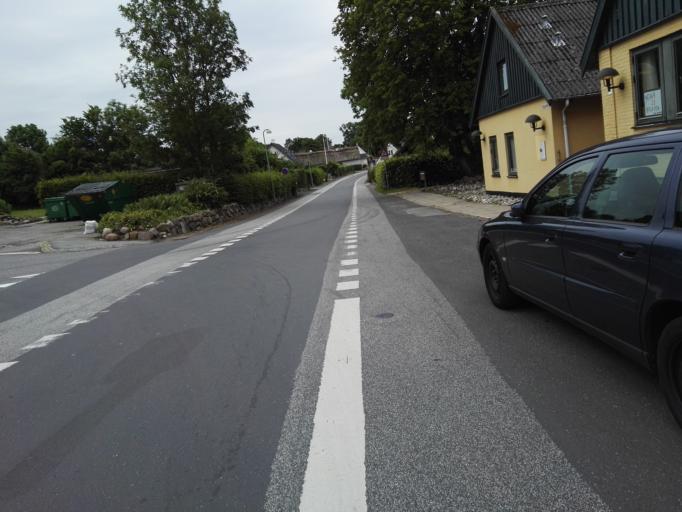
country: DK
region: Zealand
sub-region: Roskilde Kommune
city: Jyllinge
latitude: 55.7515
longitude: 12.1031
